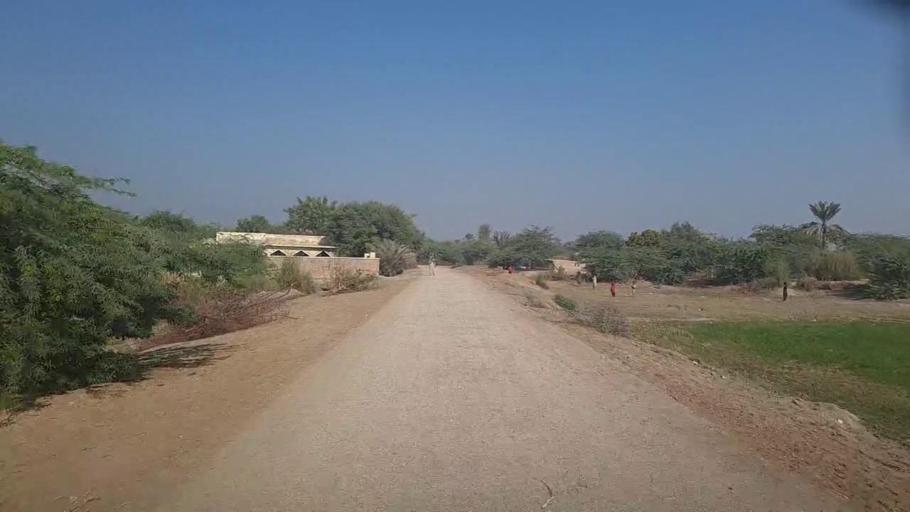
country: PK
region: Sindh
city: Kot Diji
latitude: 27.4168
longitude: 68.7057
